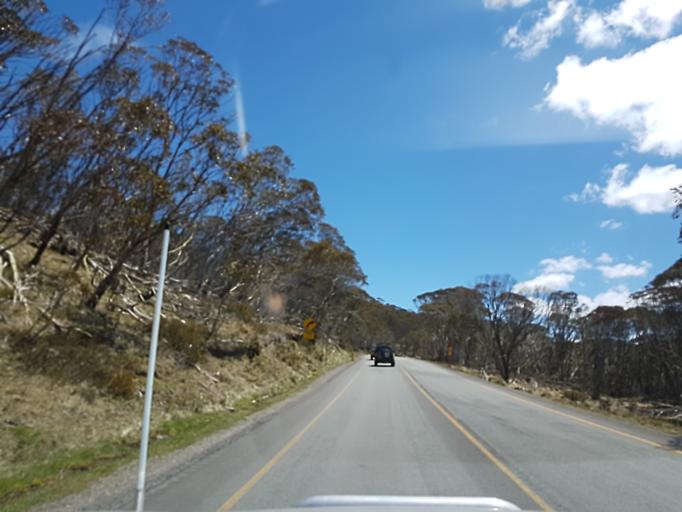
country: AU
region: Victoria
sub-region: Alpine
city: Mount Beauty
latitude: -37.0206
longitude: 147.1953
